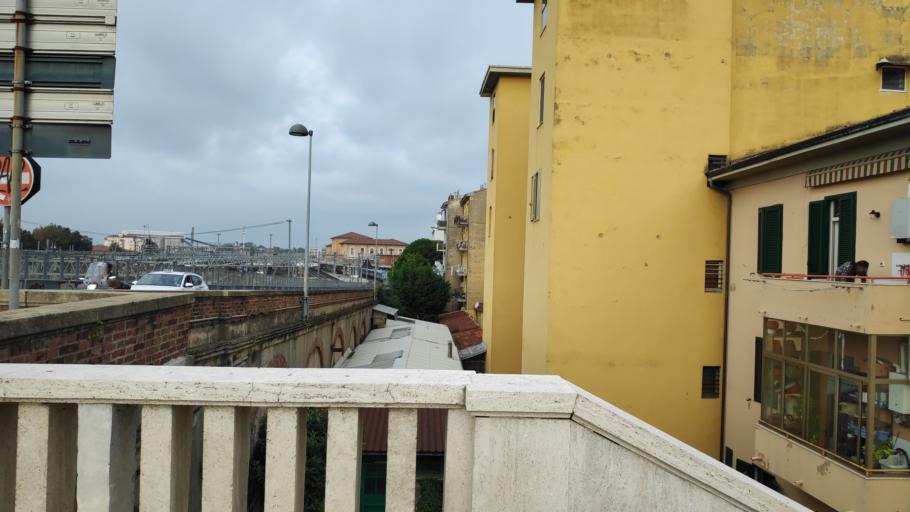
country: IT
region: Tuscany
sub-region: Province of Pisa
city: Pisa
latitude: 43.7072
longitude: 10.4032
